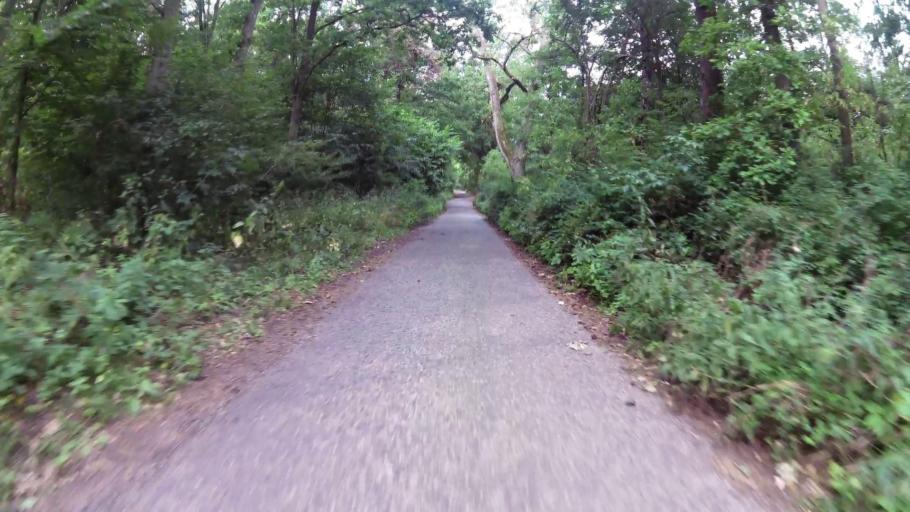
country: PL
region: West Pomeranian Voivodeship
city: Trzcinsko Zdroj
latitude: 52.8986
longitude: 14.6867
